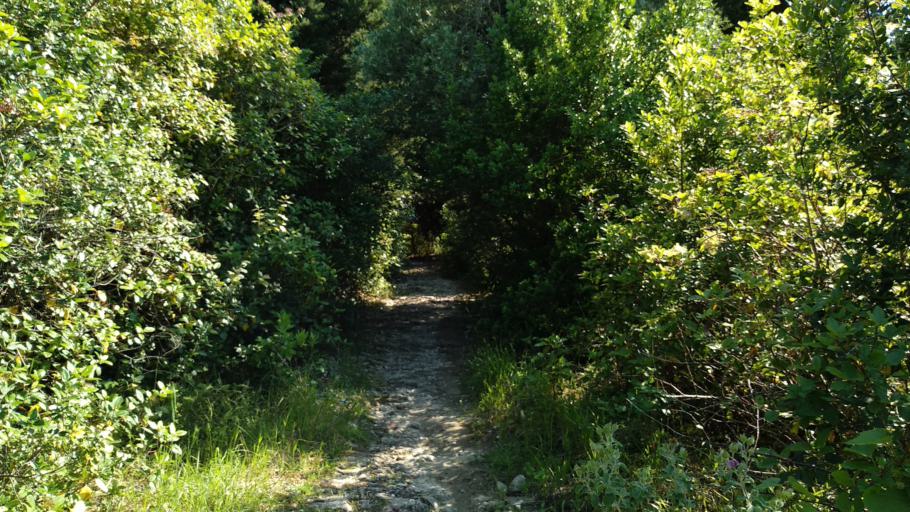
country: IT
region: Tuscany
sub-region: Provincia di Livorno
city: Quercianella
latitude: 43.4953
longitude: 10.3408
